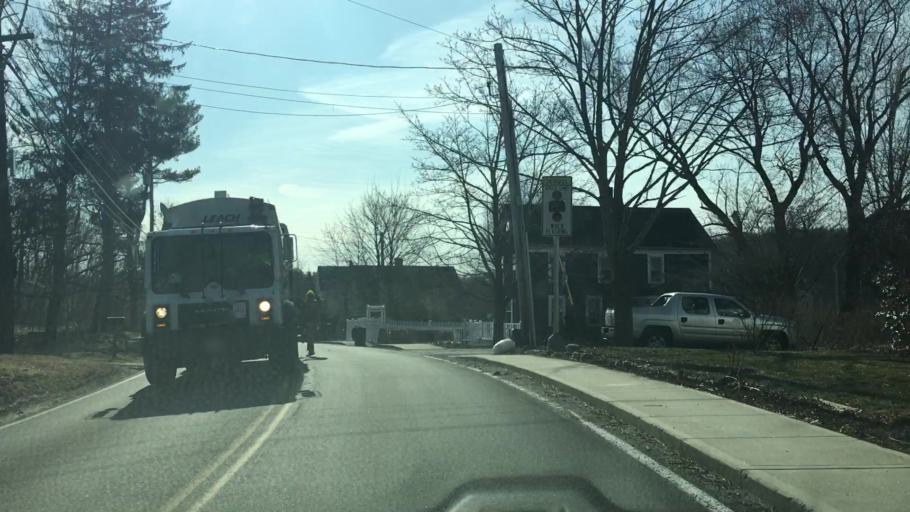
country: US
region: Massachusetts
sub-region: Essex County
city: Amesbury
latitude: 42.8555
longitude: -70.9519
